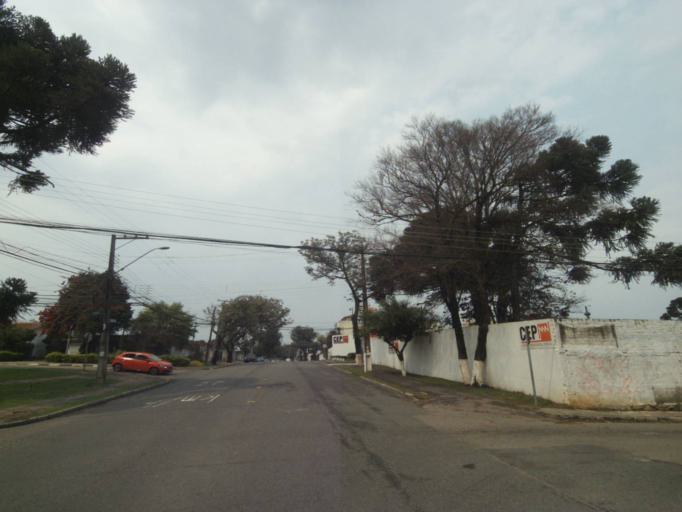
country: BR
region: Parana
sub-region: Curitiba
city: Curitiba
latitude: -25.4825
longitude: -49.2984
